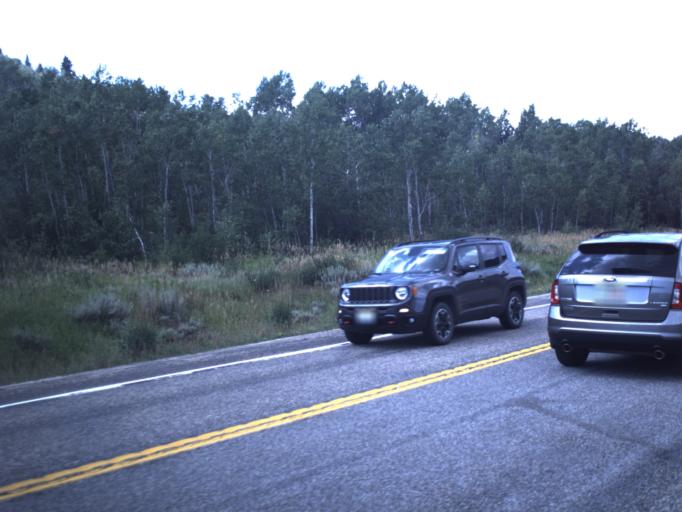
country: US
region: Utah
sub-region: Cache County
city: Richmond
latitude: 41.8746
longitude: -111.5657
